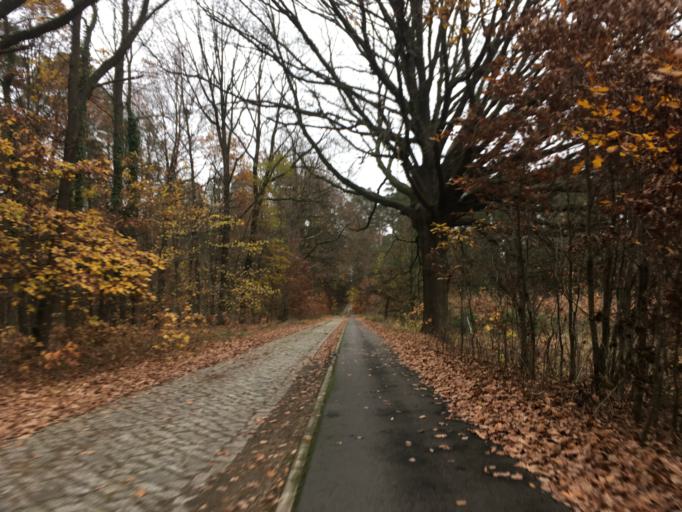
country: DE
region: Brandenburg
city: Mixdorf
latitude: 52.1495
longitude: 14.4243
